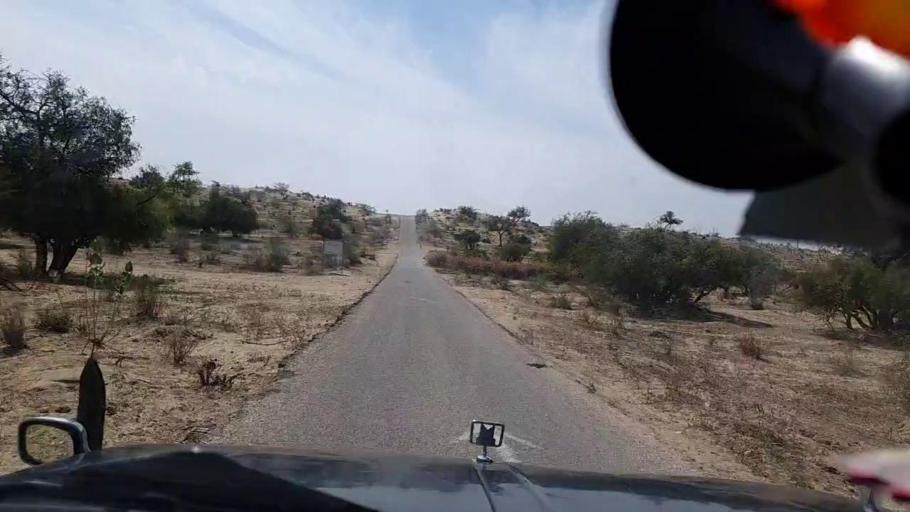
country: PK
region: Sindh
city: Diplo
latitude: 24.4200
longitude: 69.5835
